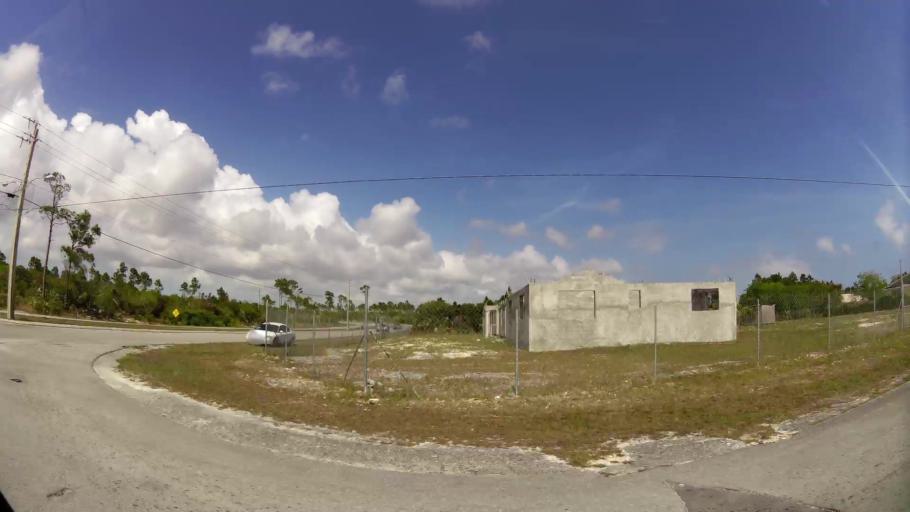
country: BS
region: Freeport
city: Freeport
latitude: 26.5038
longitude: -78.7080
